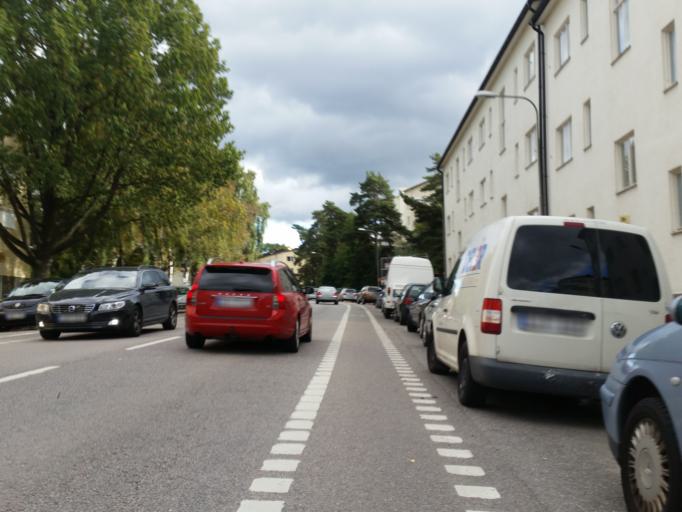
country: SE
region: Stockholm
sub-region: Stockholms Kommun
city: Arsta
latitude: 59.2980
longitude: 18.0901
